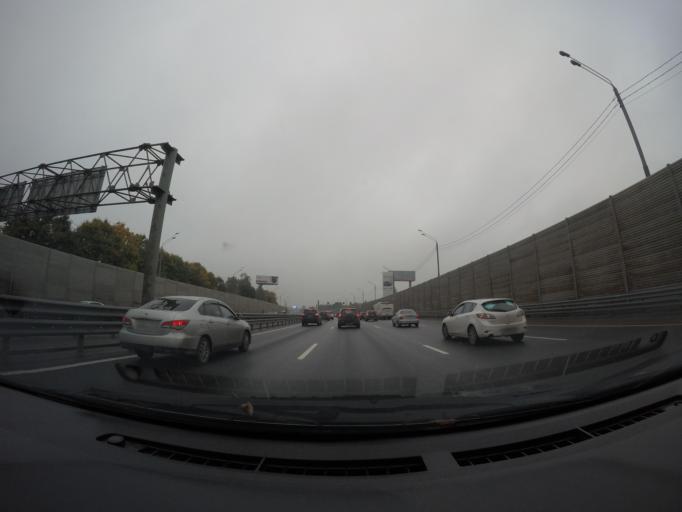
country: RU
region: Moskovskaya
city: Arkhangel'skoye
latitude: 55.7957
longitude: 37.2684
